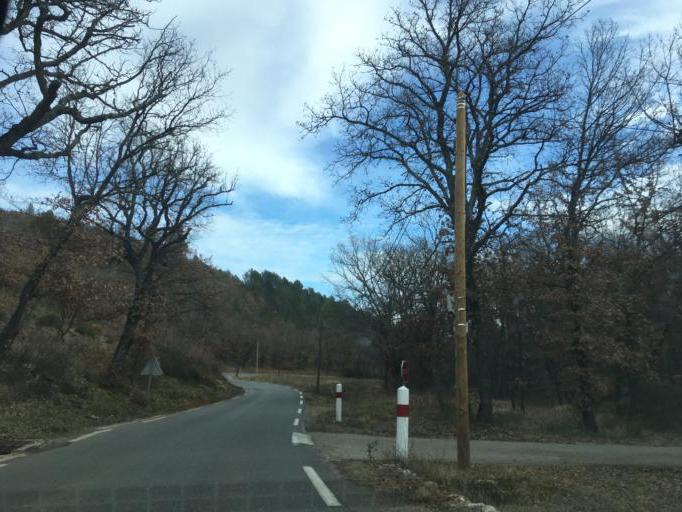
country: FR
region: Provence-Alpes-Cote d'Azur
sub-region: Departement du Var
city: Bras
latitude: 43.4605
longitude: 5.9221
